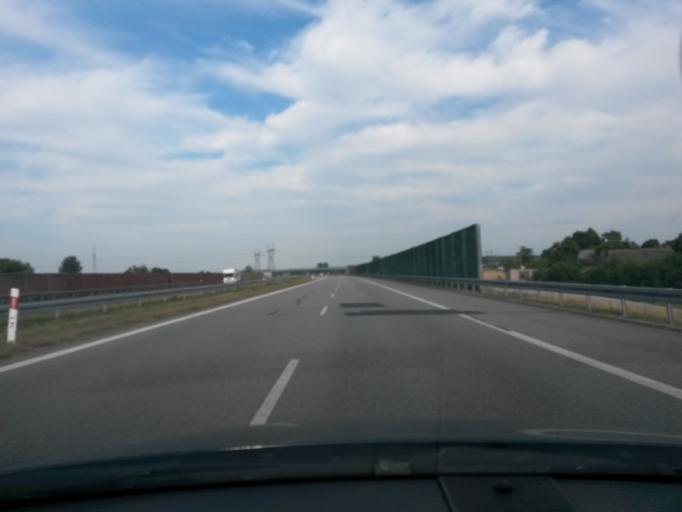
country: PL
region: Greater Poland Voivodeship
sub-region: Powiat koninski
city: Krzymow
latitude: 52.1426
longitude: 18.3976
